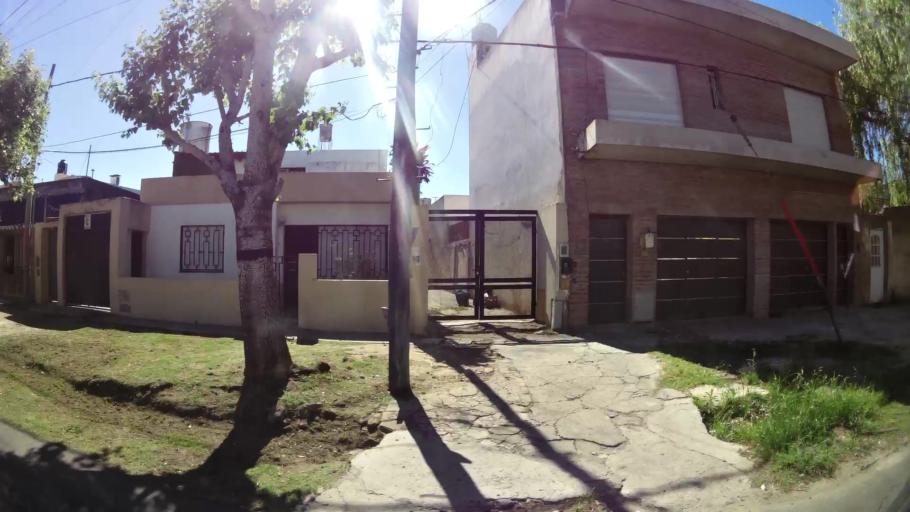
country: AR
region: Santa Fe
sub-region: Departamento de Rosario
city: Rosario
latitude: -32.9561
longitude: -60.6862
